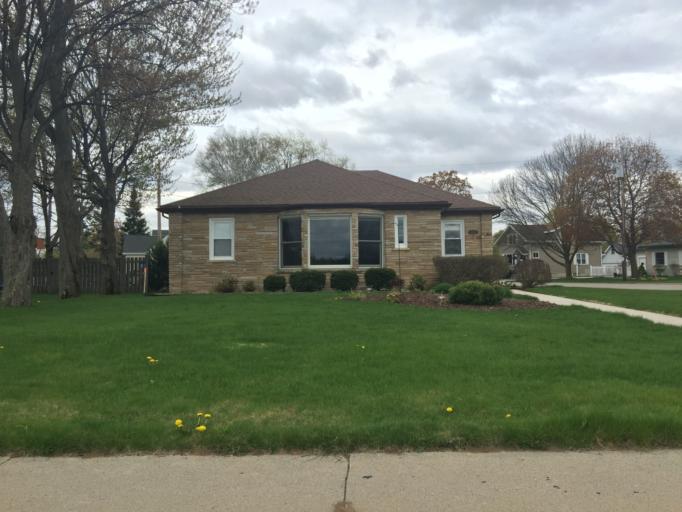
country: US
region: Wisconsin
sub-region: Marinette County
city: Marinette
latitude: 45.1044
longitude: -87.6459
